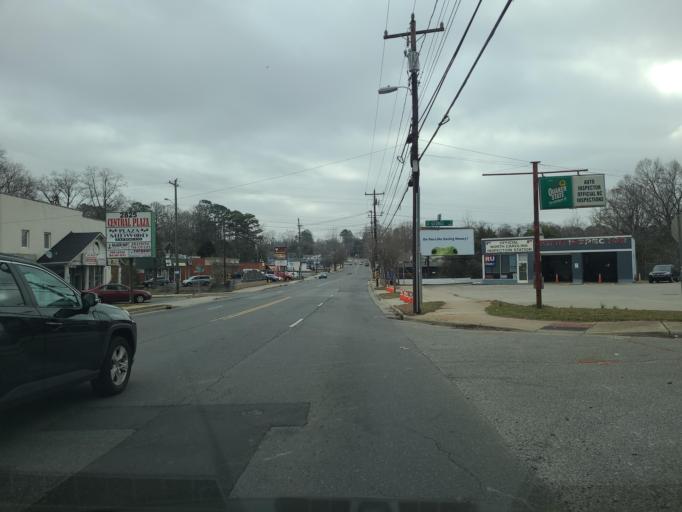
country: US
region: North Carolina
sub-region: Mecklenburg County
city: Charlotte
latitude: 35.2186
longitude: -80.7963
